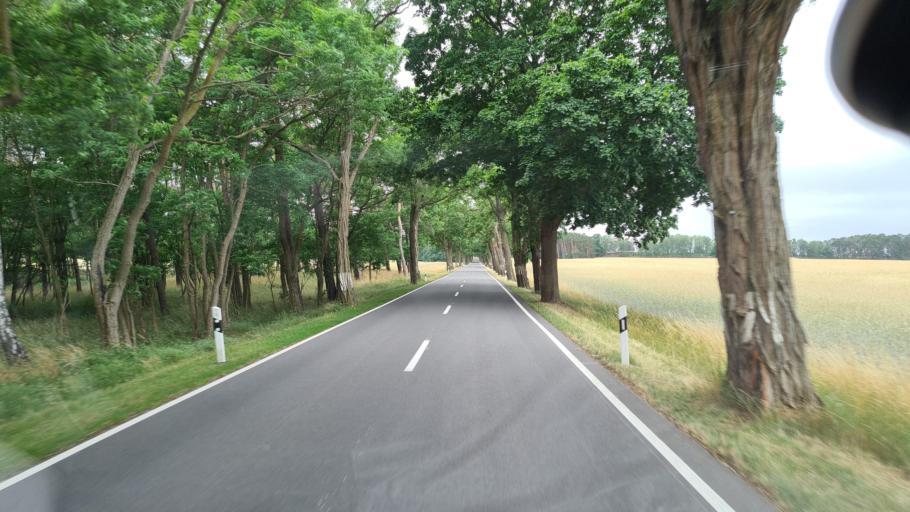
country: DE
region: Brandenburg
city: Ihlow
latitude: 51.9739
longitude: 13.2528
